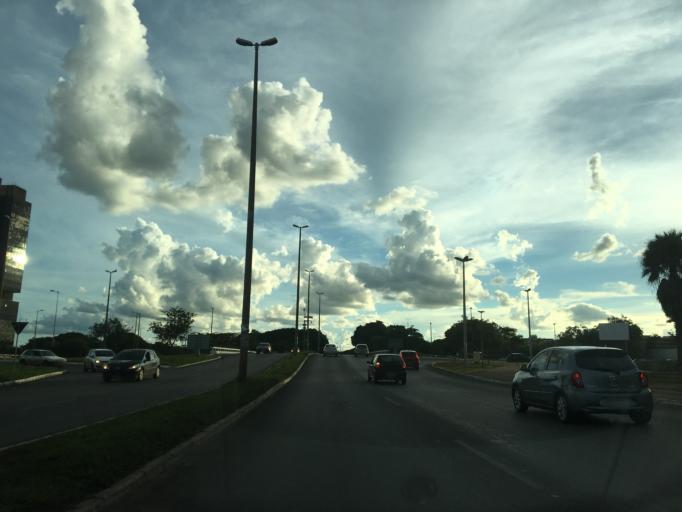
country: BR
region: Federal District
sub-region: Brasilia
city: Brasilia
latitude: -15.7995
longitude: -47.8856
